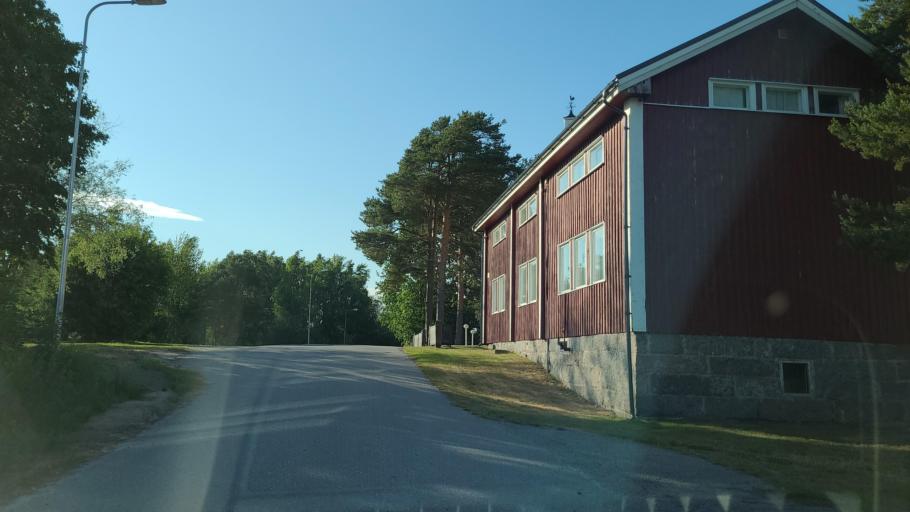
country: FI
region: Ostrobothnia
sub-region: Vaasa
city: Replot
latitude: 63.3463
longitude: 21.3336
